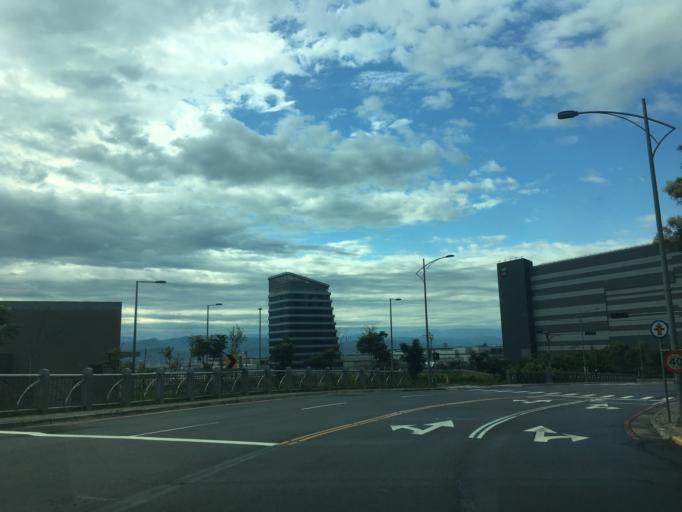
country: TW
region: Taiwan
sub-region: Taichung City
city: Taichung
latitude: 24.2119
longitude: 120.6088
